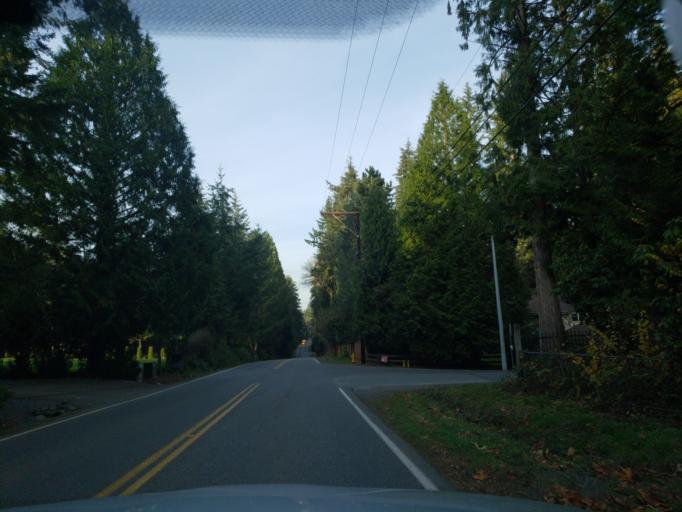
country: US
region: Washington
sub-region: Snohomish County
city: Maltby
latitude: 47.7864
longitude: -122.1327
